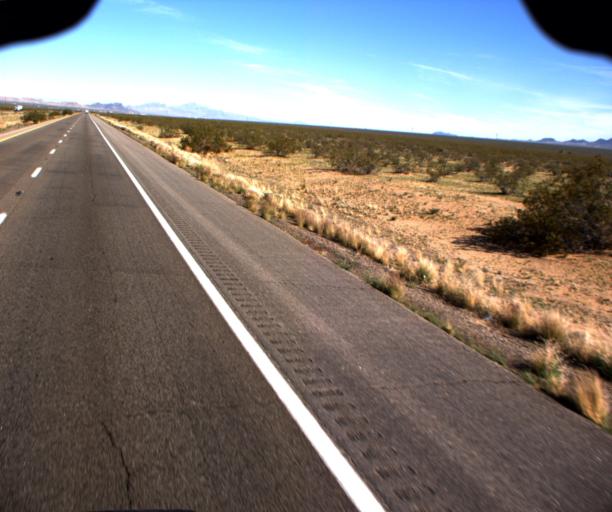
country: US
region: Arizona
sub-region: Mohave County
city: Dolan Springs
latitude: 35.6407
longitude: -114.4341
